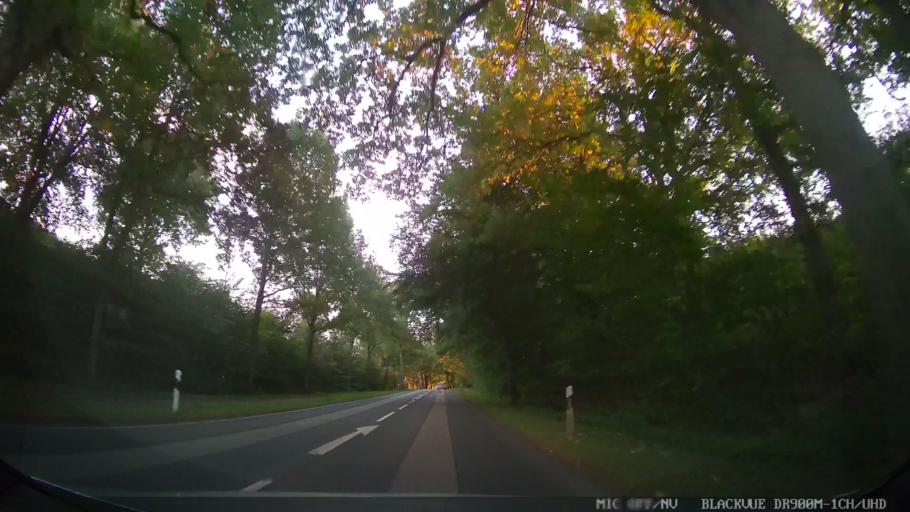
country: DE
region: Schleswig-Holstein
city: Susel
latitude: 54.0199
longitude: 10.6851
